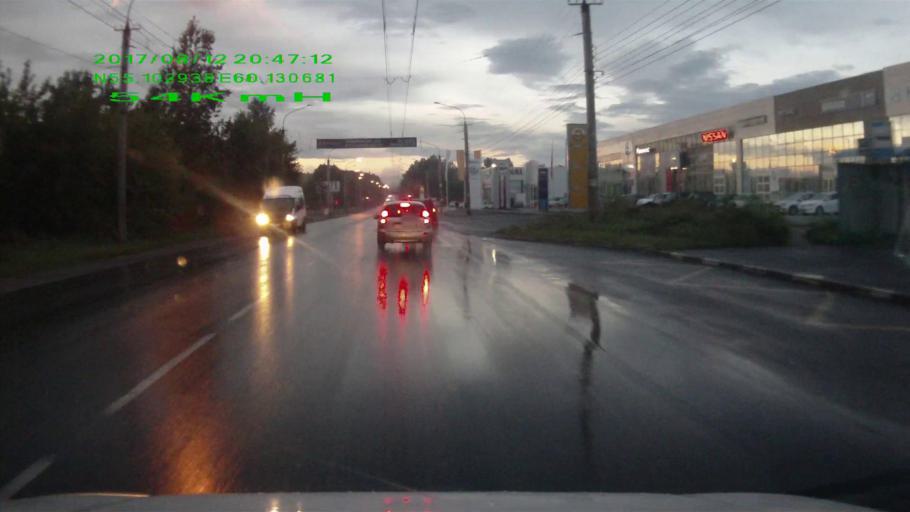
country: RU
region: Chelyabinsk
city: Turgoyak
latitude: 55.1033
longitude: 60.1307
